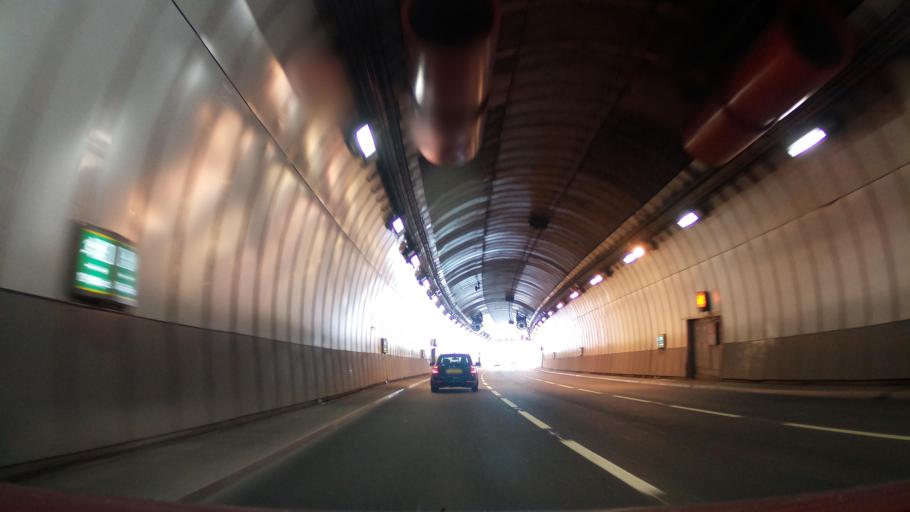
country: GB
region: England
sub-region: Cornwall
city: Saltash
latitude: 50.4113
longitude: -4.2152
